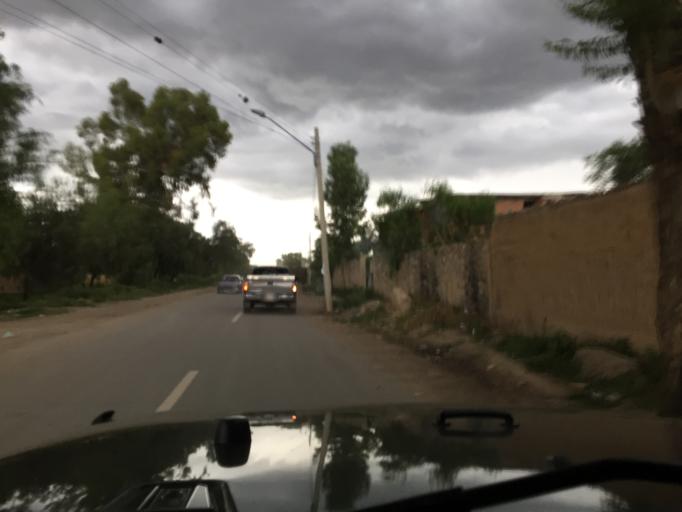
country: BO
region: Cochabamba
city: Cochabamba
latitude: -17.3999
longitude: -66.2039
